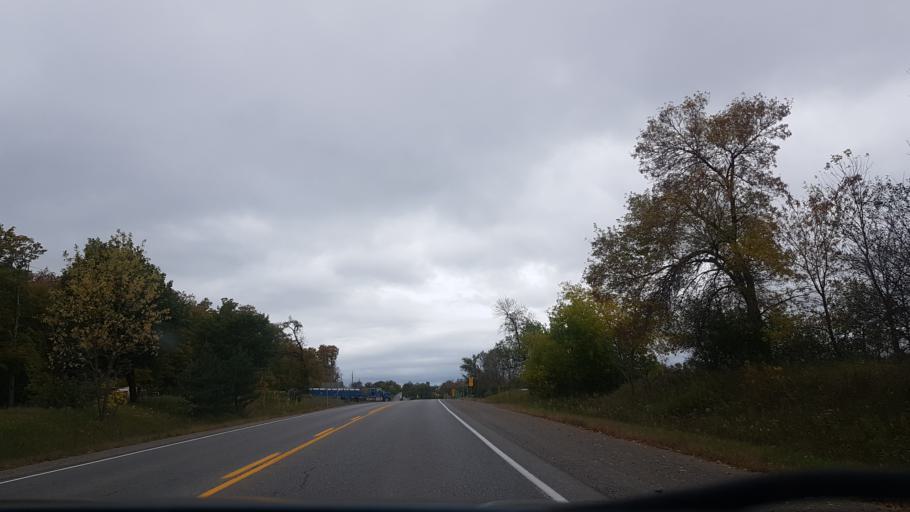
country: CA
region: Ontario
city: Peterborough
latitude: 44.2557
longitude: -78.4010
